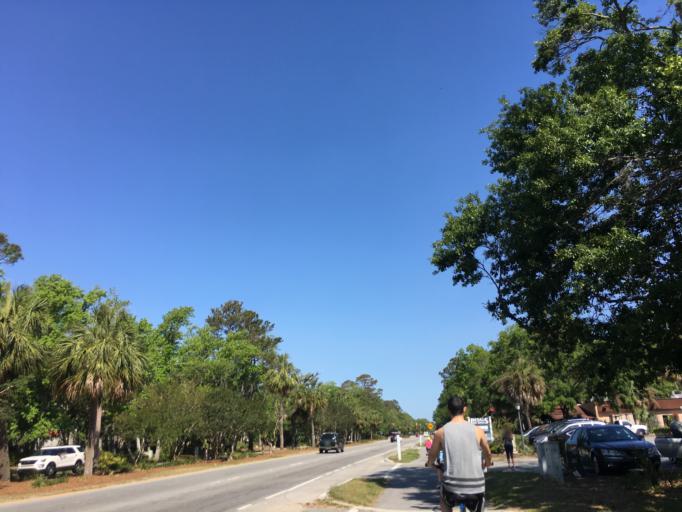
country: US
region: South Carolina
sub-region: Beaufort County
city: Hilton Head Island
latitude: 32.1453
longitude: -80.7538
